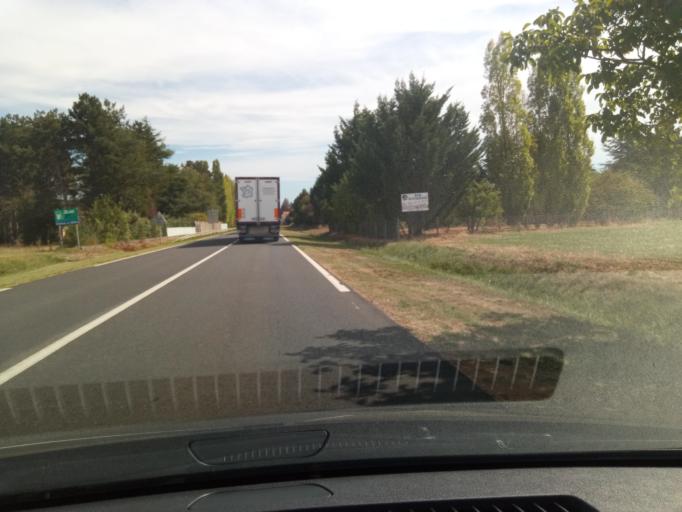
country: FR
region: Poitou-Charentes
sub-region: Departement de la Vienne
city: Terce
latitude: 46.4819
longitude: 0.5143
